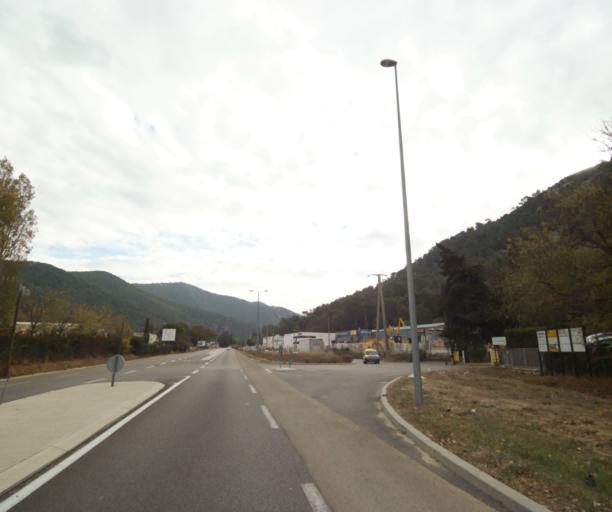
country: FR
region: Provence-Alpes-Cote d'Azur
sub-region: Departement des Bouches-du-Rhone
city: Gemenos
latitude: 43.2770
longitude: 5.6248
